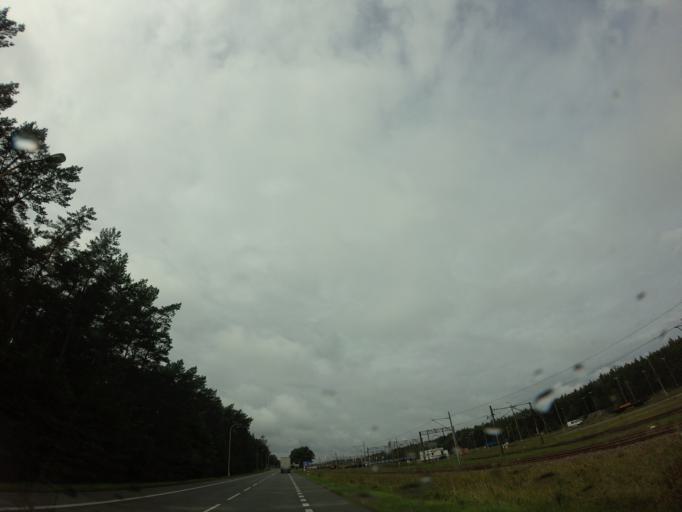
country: PL
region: West Pomeranian Voivodeship
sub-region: Swinoujscie
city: Swinoujscie
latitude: 53.8975
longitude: 14.3316
